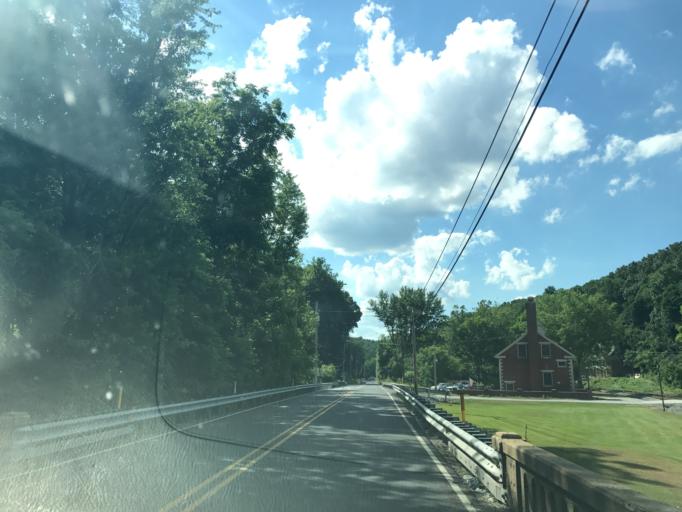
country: US
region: Pennsylvania
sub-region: York County
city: Glen Rock
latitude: 39.7692
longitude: -76.8261
